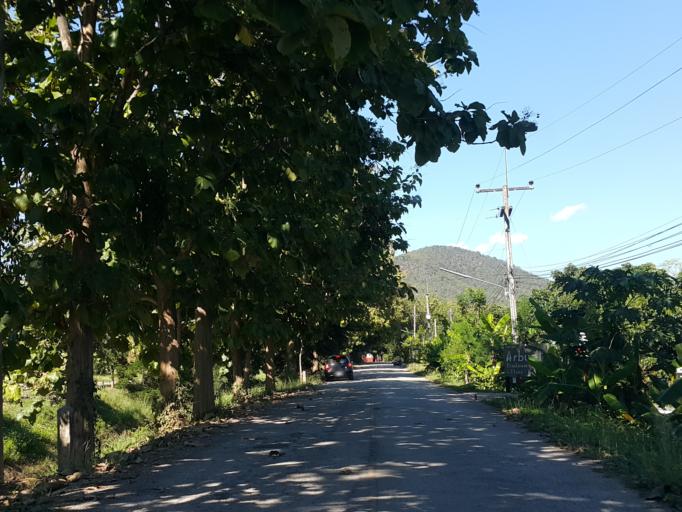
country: TH
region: Chiang Mai
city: San Sai
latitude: 18.9128
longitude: 99.1294
